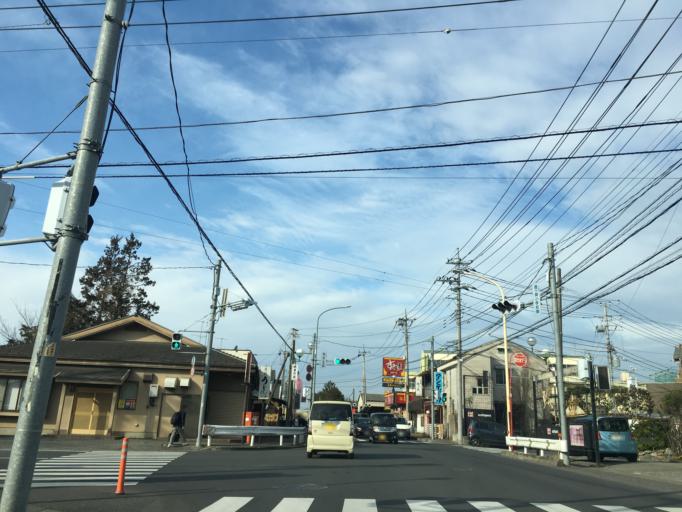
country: JP
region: Saitama
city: Sakado
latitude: 35.9125
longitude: 139.4240
